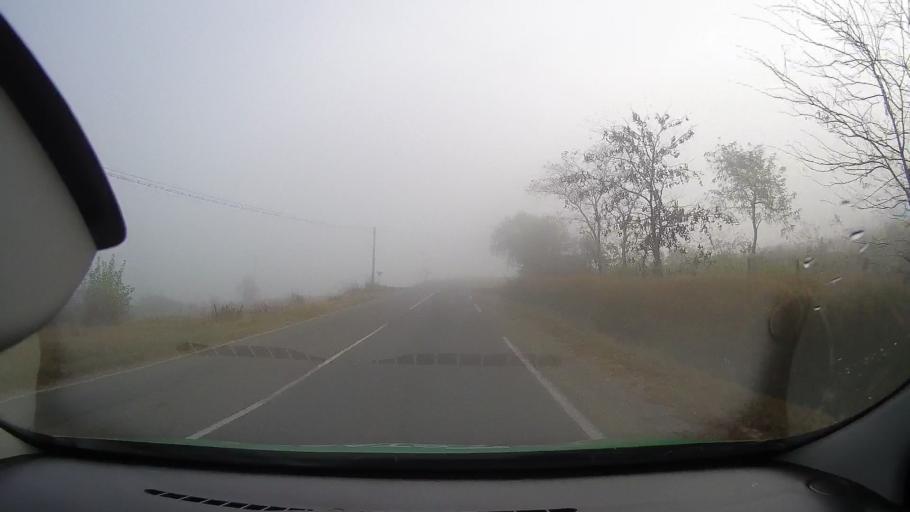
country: RO
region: Tulcea
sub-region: Municipiul Tulcea
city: Tulcea
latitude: 45.1660
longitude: 28.8417
